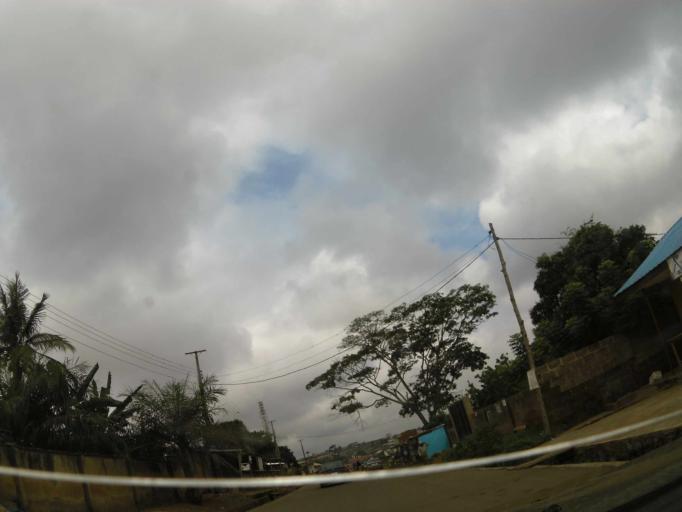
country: NG
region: Oyo
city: Ibadan
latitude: 7.4366
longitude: 3.9485
